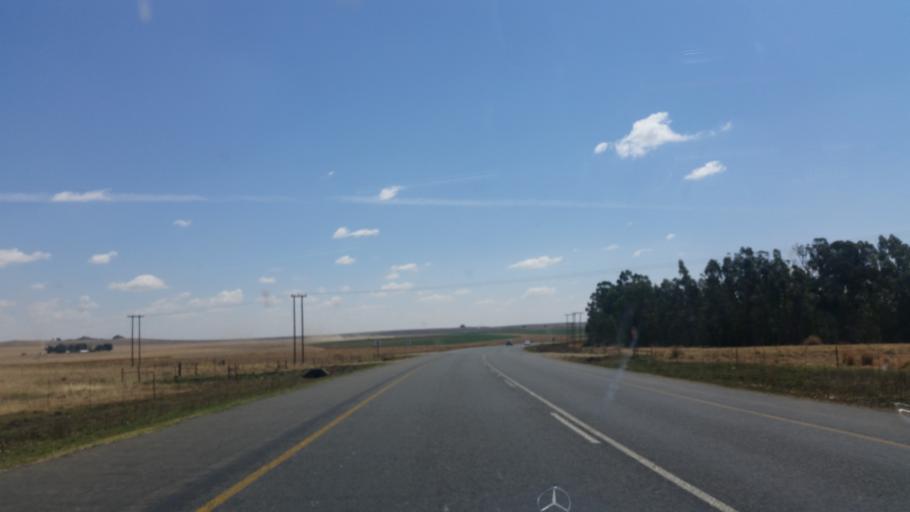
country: ZA
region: Orange Free State
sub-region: Thabo Mofutsanyana District Municipality
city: Bethlehem
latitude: -28.1061
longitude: 28.6628
